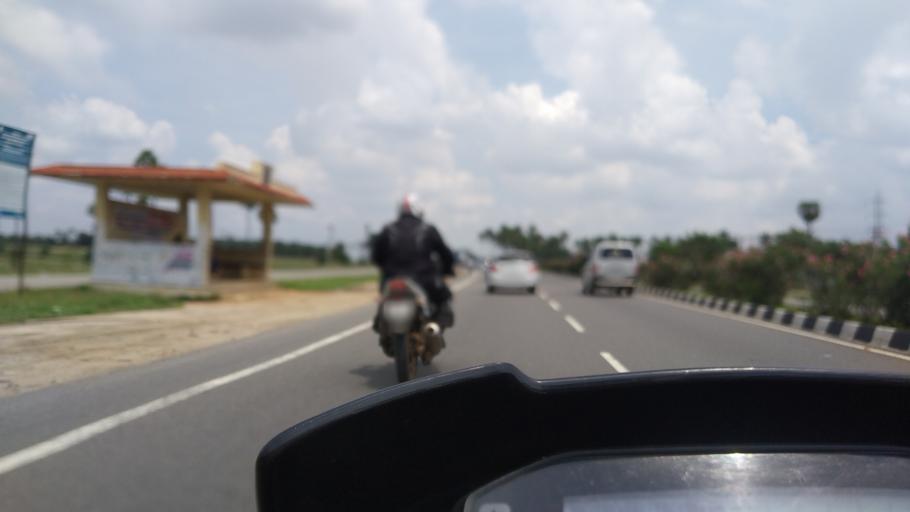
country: IN
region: Tamil Nadu
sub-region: Erode
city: Vijayapuri
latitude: 11.2500
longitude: 77.5361
